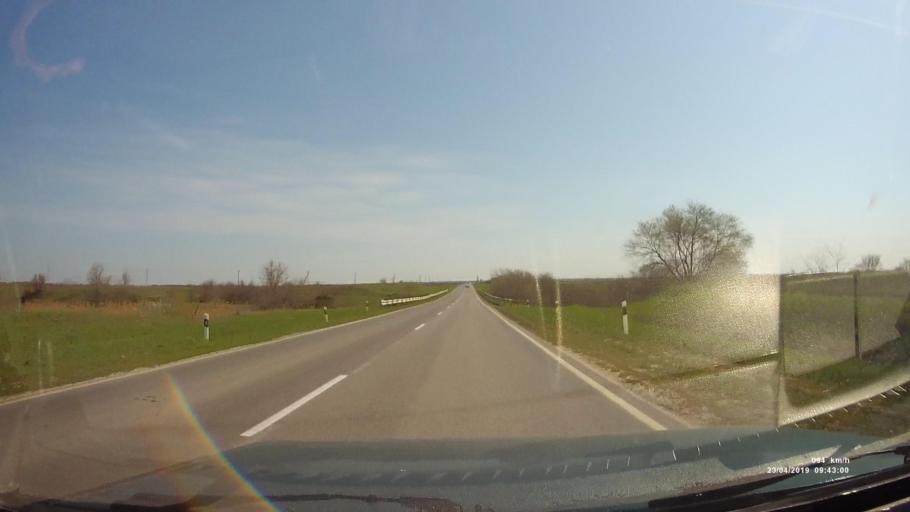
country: RU
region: Rostov
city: Orlovskiy
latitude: 46.8727
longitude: 41.9878
